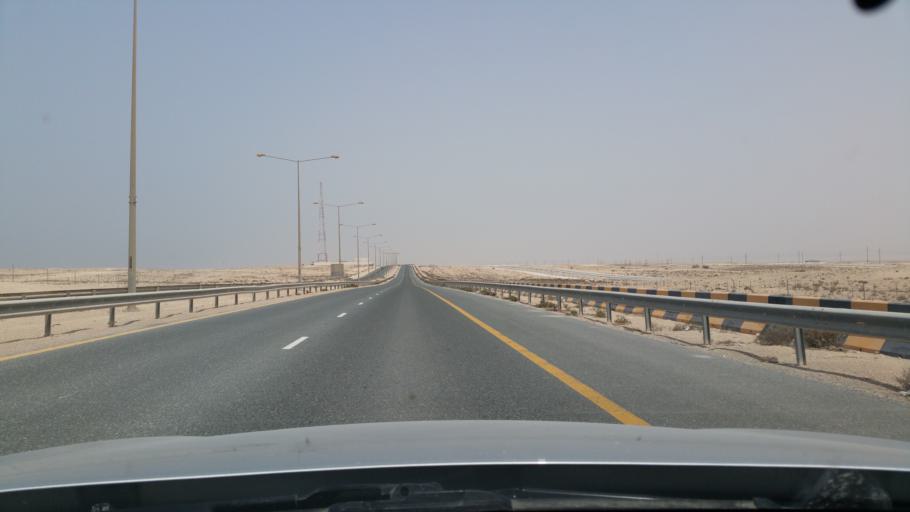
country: QA
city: Umm Bab
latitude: 25.3041
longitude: 50.7925
